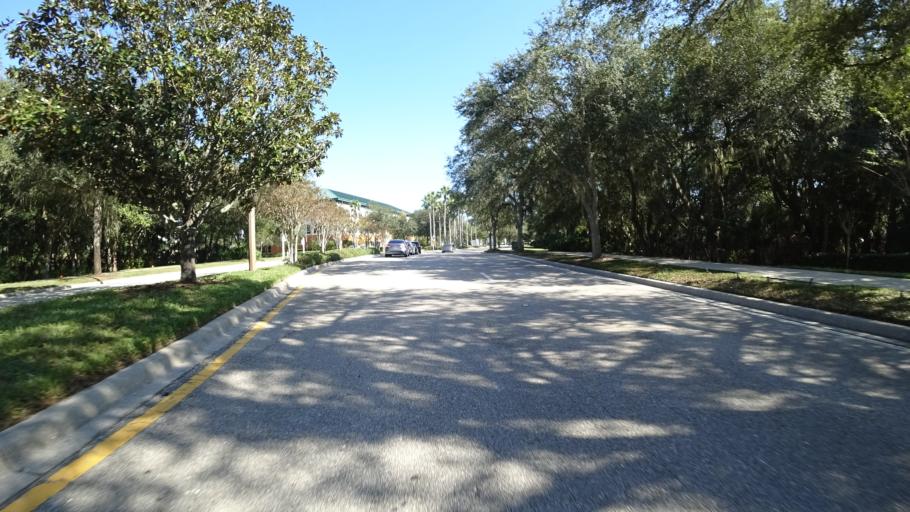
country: US
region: Florida
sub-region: Sarasota County
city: The Meadows
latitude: 27.3907
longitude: -82.4386
